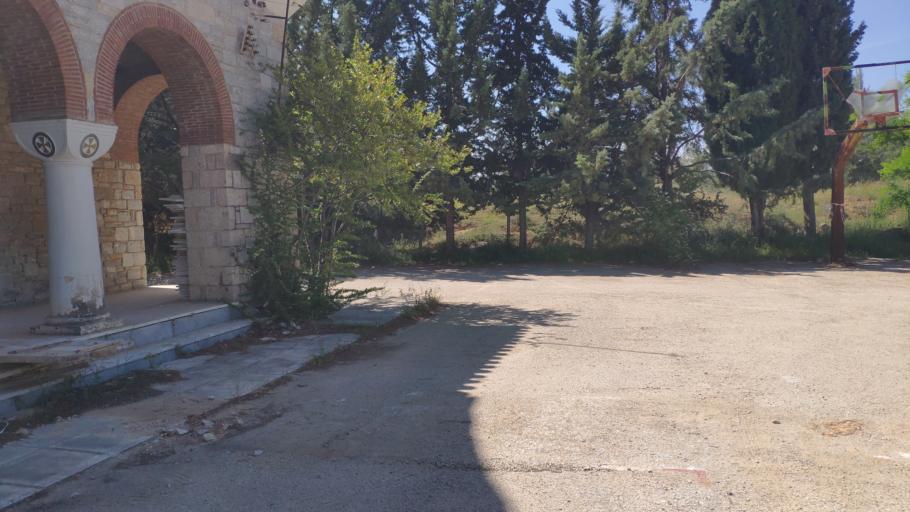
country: GR
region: Attica
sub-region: Nomarchia Athinas
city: Metamorfosi
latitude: 38.0790
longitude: 23.7708
